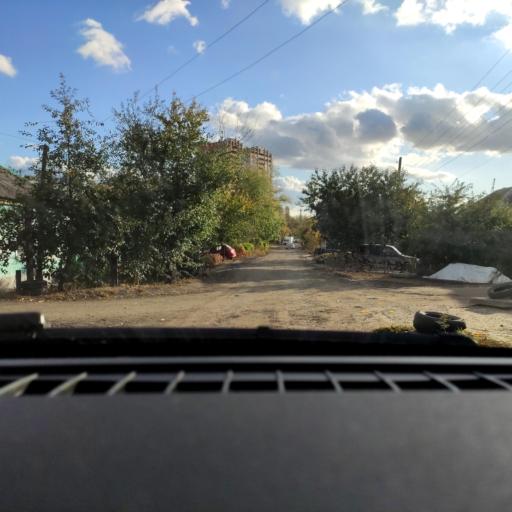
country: RU
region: Voronezj
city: Voronezh
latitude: 51.6648
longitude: 39.2841
